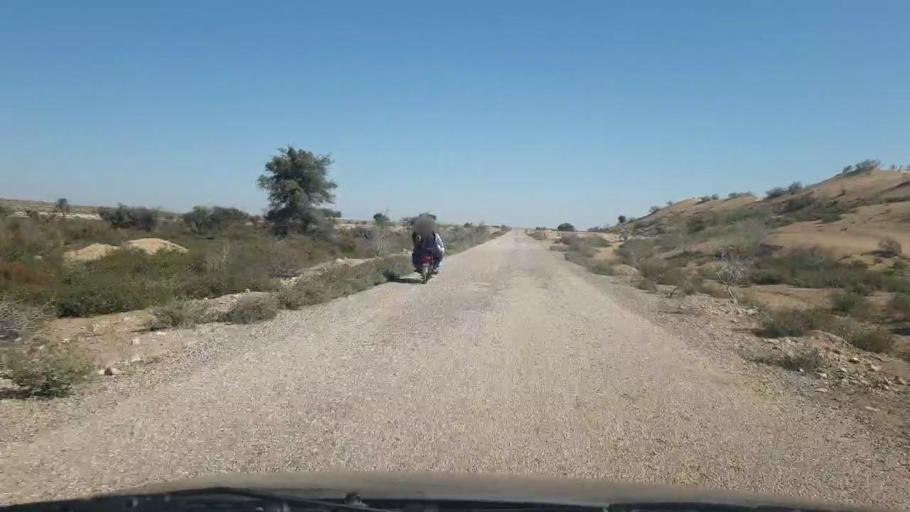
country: PK
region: Sindh
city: Bozdar
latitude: 27.0152
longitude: 68.7486
